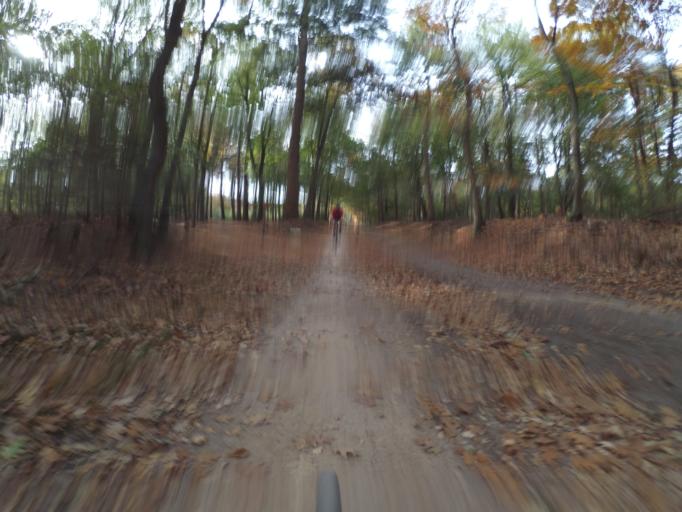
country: NL
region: Overijssel
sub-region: Gemeente Twenterand
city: Den Ham
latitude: 52.3646
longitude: 6.4258
